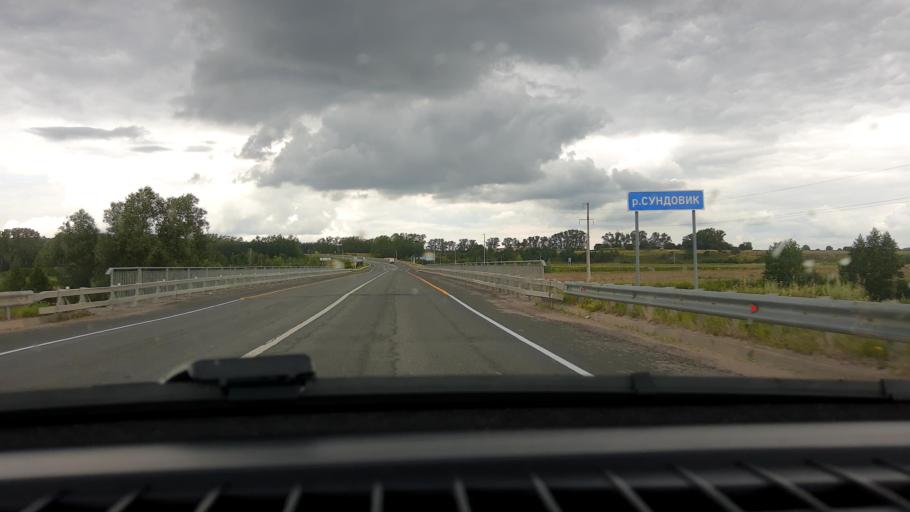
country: RU
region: Nizjnij Novgorod
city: Bol'shoye Murashkino
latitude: 55.8797
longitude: 44.7480
